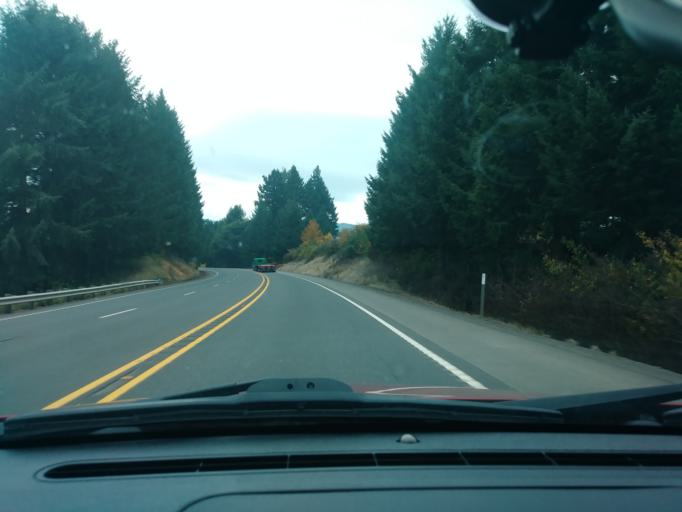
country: US
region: Oregon
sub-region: Washington County
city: Banks
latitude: 45.6200
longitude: -123.2200
